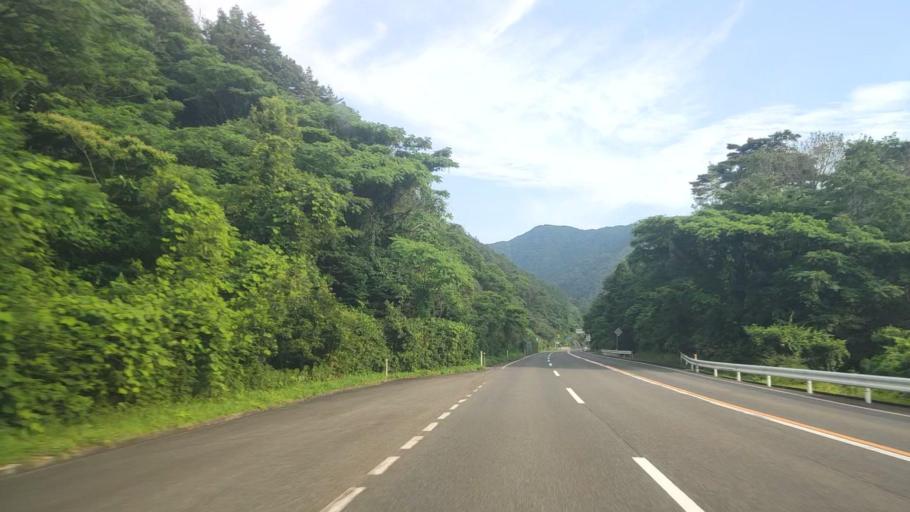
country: JP
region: Tottori
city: Kurayoshi
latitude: 35.3248
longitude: 133.7563
